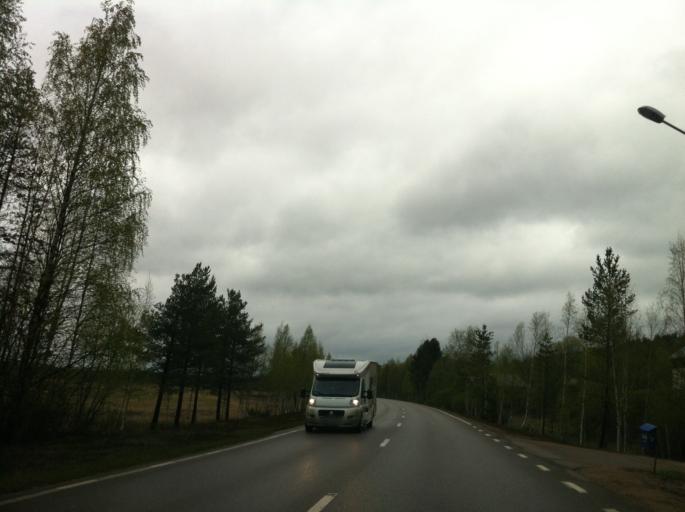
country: SE
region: Jaemtland
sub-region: Harjedalens Kommun
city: Sveg
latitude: 62.1269
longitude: 14.0677
